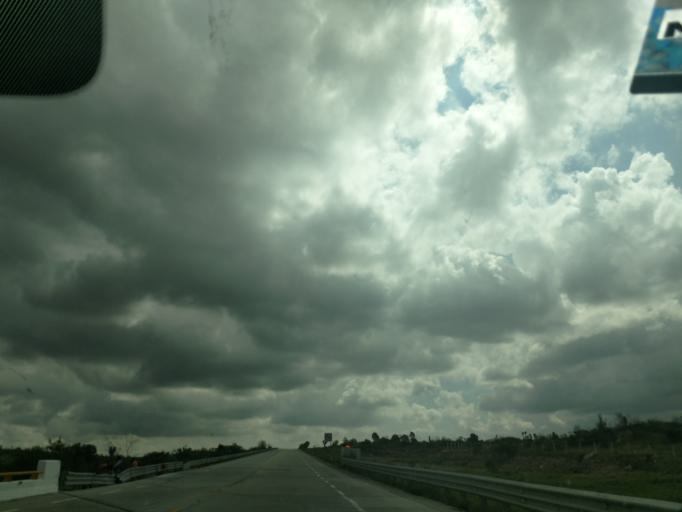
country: MX
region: Jalisco
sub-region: Ojuelos de Jalisco
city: Matanzas
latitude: 21.5611
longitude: -101.6859
